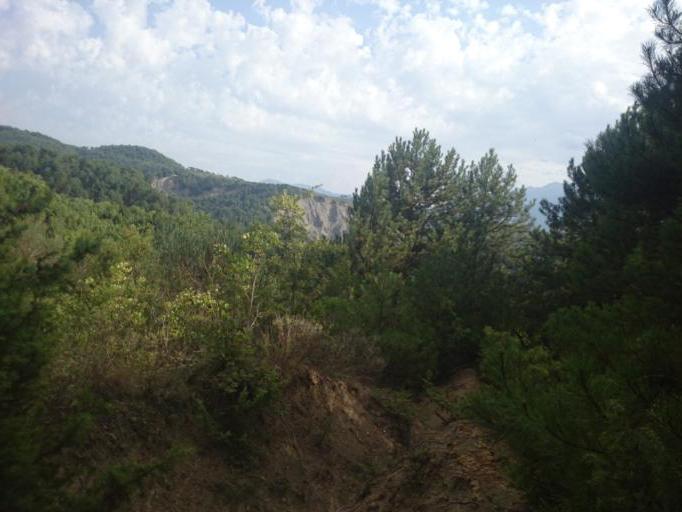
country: AL
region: Elbasan
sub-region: Rrethi i Gramshit
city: Skenderbegas
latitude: 40.7591
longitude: 20.2292
